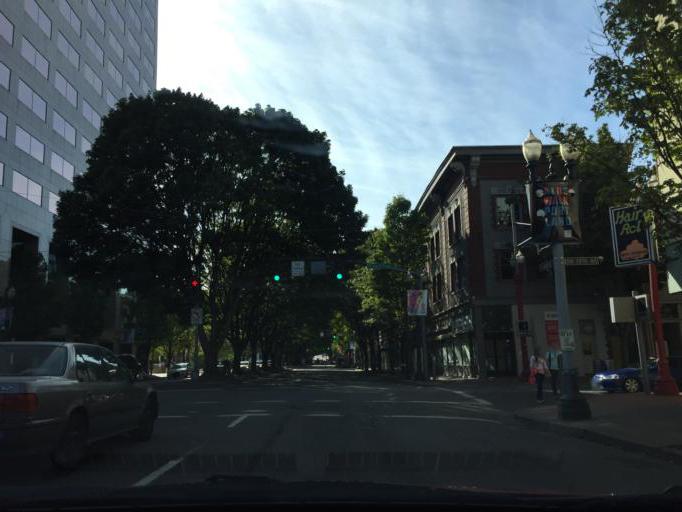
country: US
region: Oregon
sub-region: Multnomah County
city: Portland
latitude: 45.5231
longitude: -122.6751
